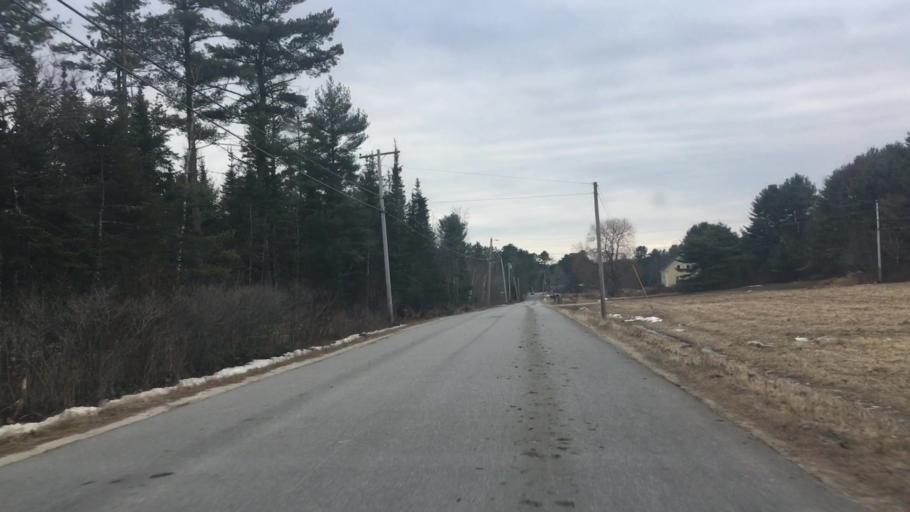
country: US
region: Maine
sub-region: Cumberland County
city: Freeport
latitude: 43.8353
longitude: -70.0776
